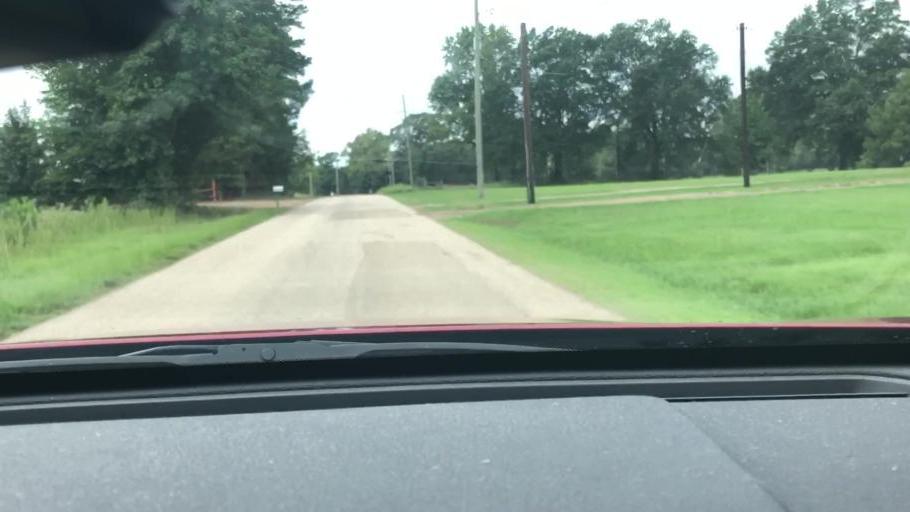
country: US
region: Texas
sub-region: Bowie County
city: Wake Village
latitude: 33.3758
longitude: -94.0968
